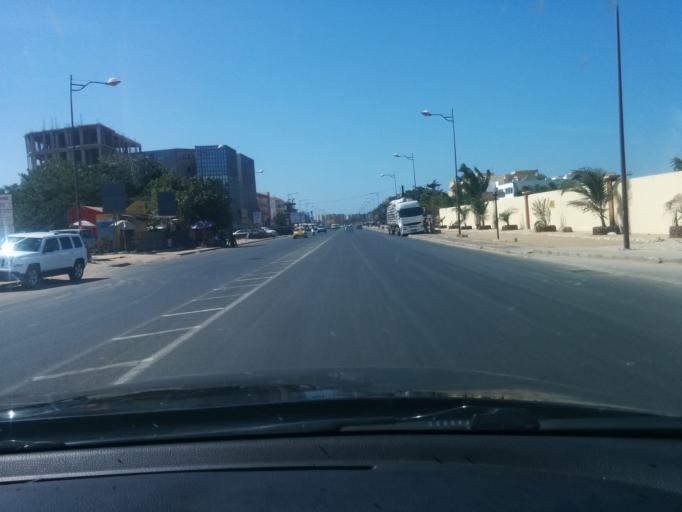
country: SN
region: Dakar
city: Mermoz Boabab
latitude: 14.7130
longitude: -17.4759
